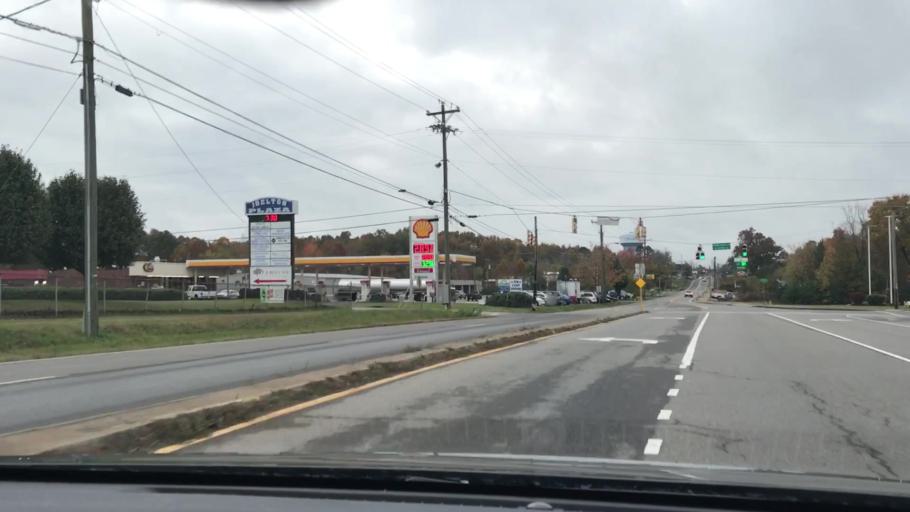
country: US
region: Tennessee
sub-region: Robertson County
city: Ridgetop
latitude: 36.3217
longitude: -86.8677
